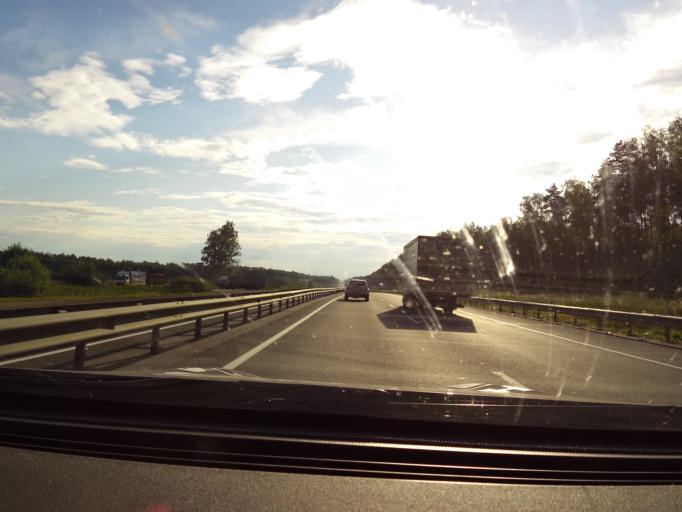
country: RU
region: Vladimir
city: Melekhovo
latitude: 56.2076
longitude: 41.2204
